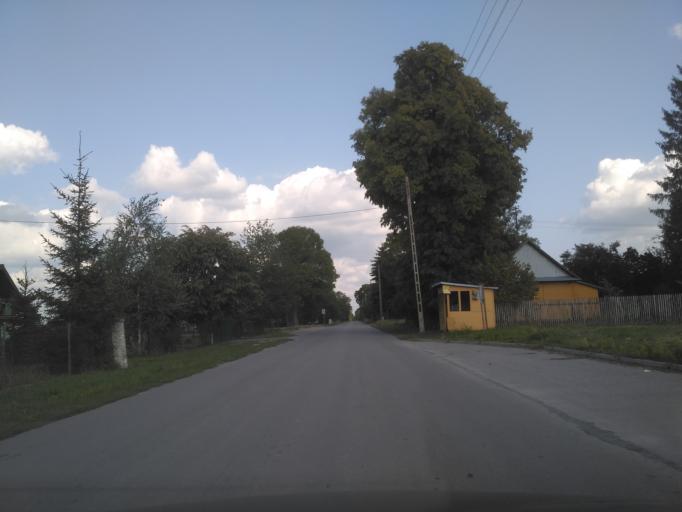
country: PL
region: Lublin Voivodeship
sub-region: Powiat chelmski
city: Pokrowka
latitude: 51.0681
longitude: 23.4901
